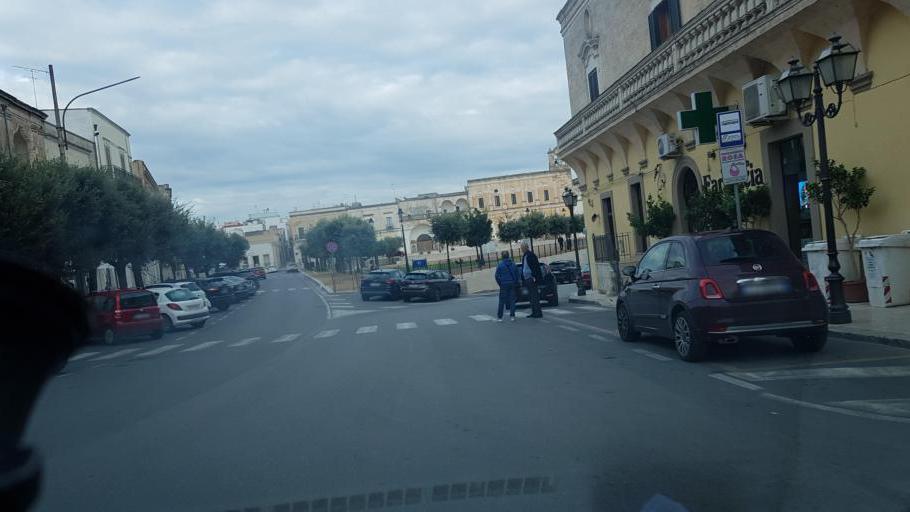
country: IT
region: Apulia
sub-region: Provincia di Brindisi
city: Oria
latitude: 40.4965
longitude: 17.6436
